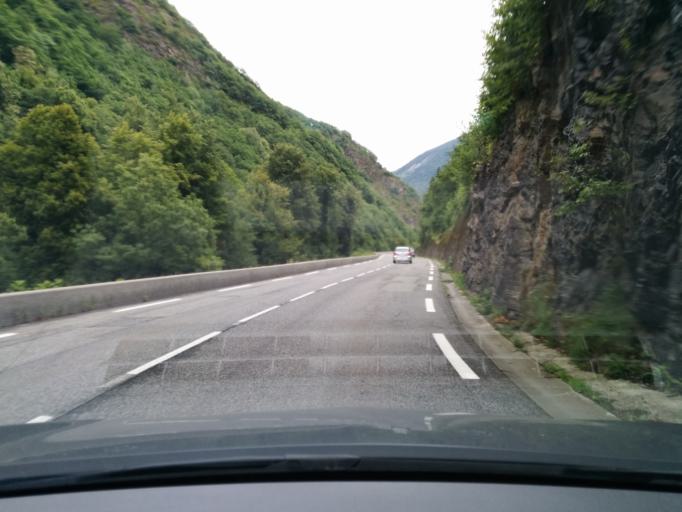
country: FR
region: Midi-Pyrenees
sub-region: Departement des Hautes-Pyrenees
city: Saint-Lary-Soulan
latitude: 42.7986
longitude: 0.2777
